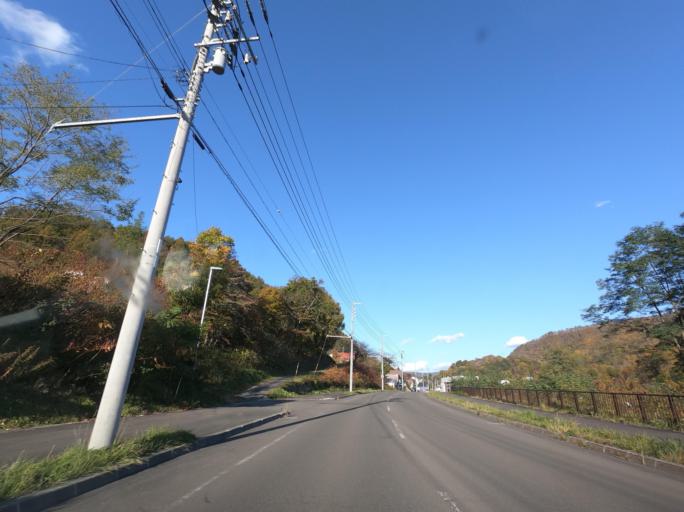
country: JP
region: Hokkaido
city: Iwamizawa
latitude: 43.0546
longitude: 141.9692
